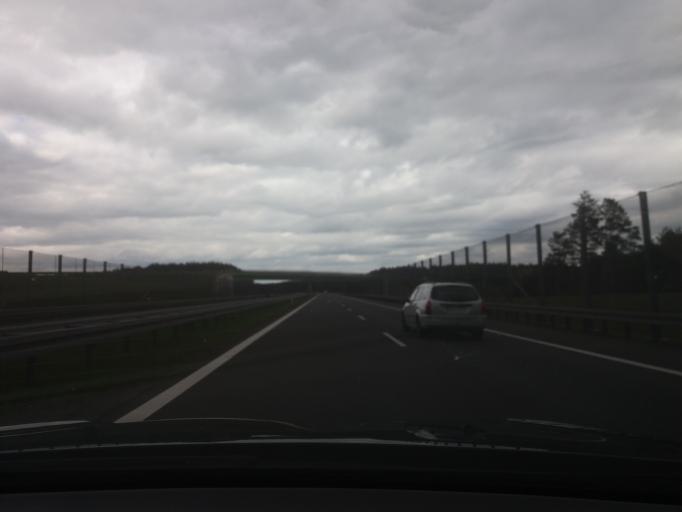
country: PL
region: Lubusz
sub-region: Powiat miedzyrzecki
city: Skwierzyna
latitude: 52.5680
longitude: 15.4724
